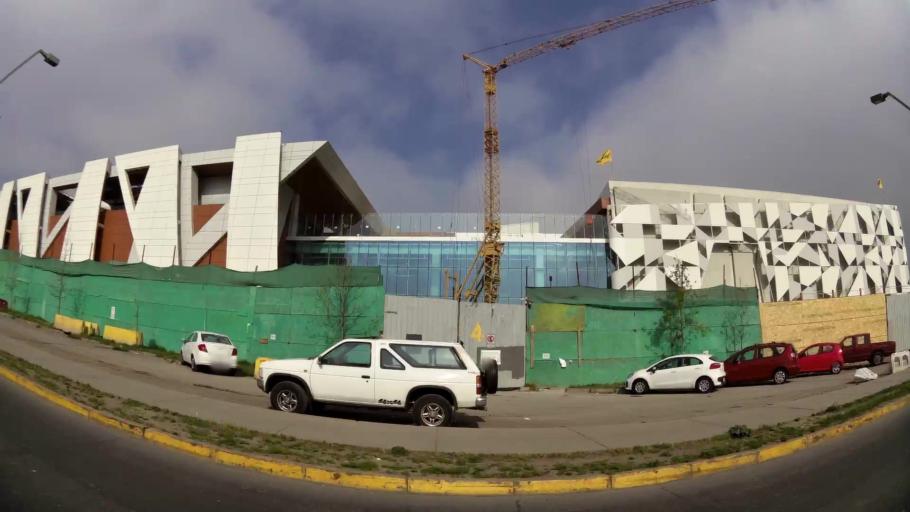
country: CL
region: Santiago Metropolitan
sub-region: Provincia de Santiago
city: Villa Presidente Frei, Nunoa, Santiago, Chile
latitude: -33.4147
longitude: -70.5395
